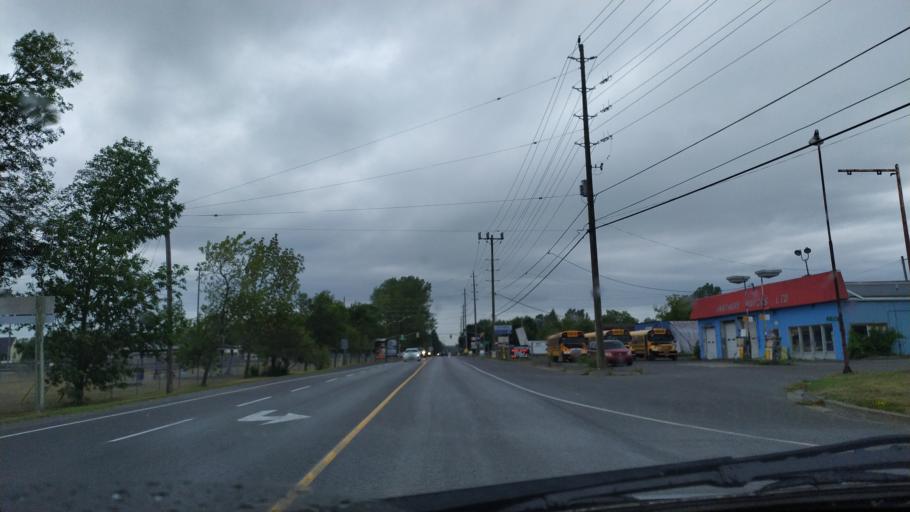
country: CA
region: Ontario
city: Quinte West
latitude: 44.0479
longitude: -77.5797
